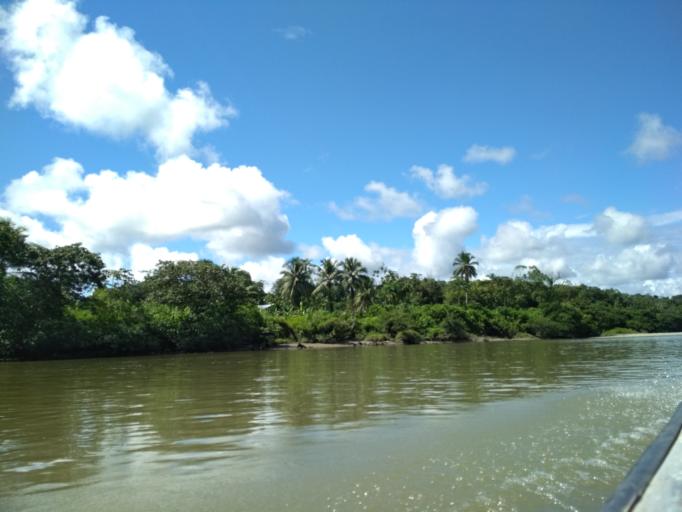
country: CO
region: Cauca
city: Timbiqui
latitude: 2.7637
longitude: -77.6633
